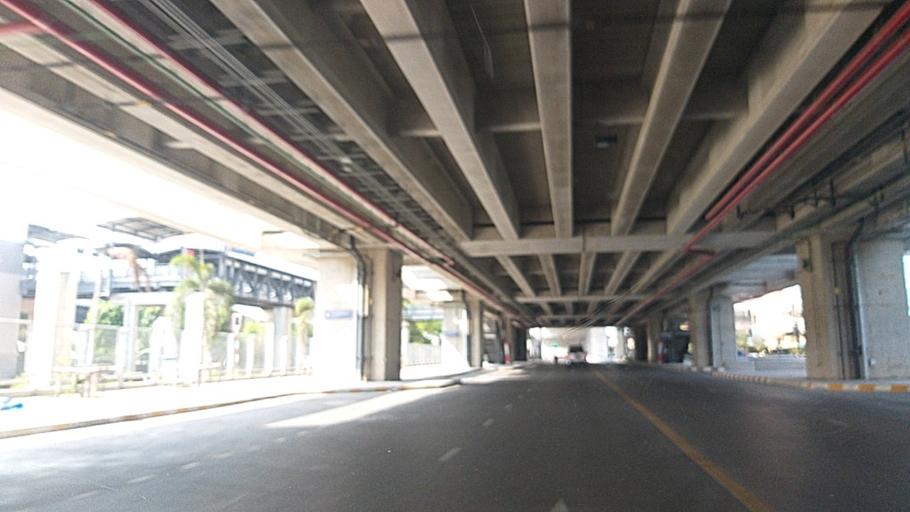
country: TH
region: Bangkok
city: Chatuchak
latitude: 13.8419
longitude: 100.5577
